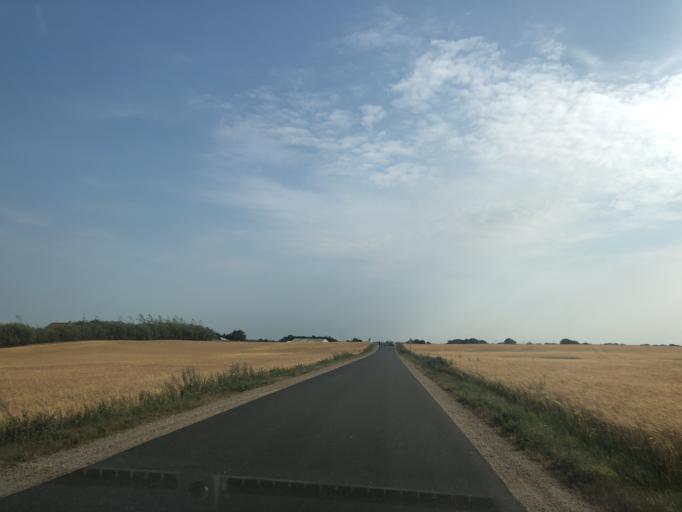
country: DK
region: North Denmark
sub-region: Morso Kommune
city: Nykobing Mors
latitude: 56.8244
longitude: 9.0191
